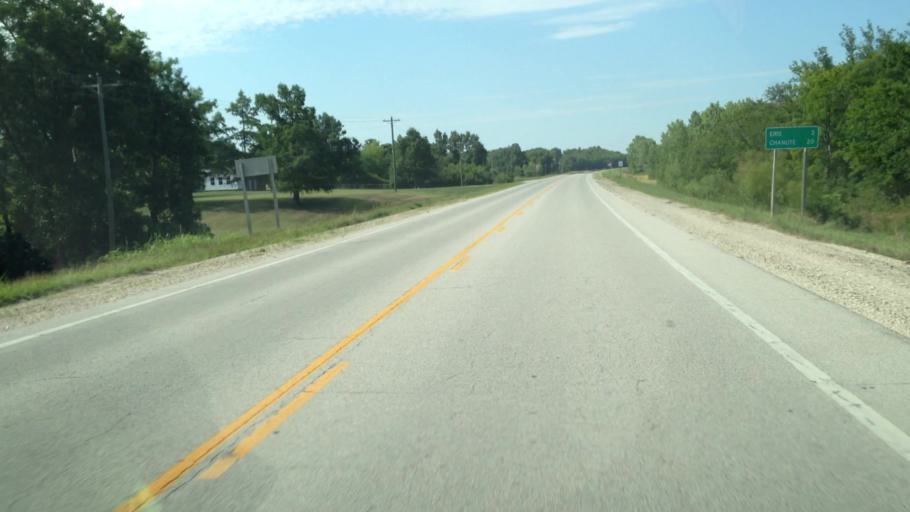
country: US
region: Kansas
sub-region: Neosho County
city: Erie
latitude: 37.5301
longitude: -95.2703
